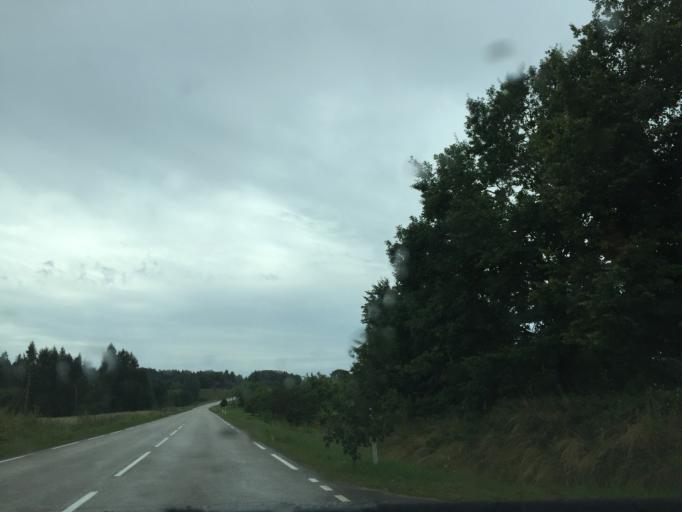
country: LV
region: Preilu Rajons
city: Jaunaglona
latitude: 56.2500
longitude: 27.2162
